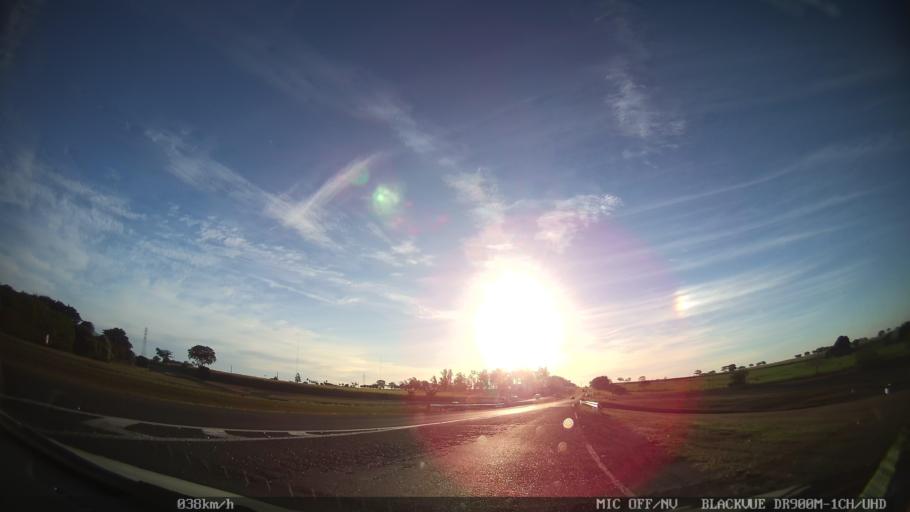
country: BR
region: Sao Paulo
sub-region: Guapiacu
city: Guapiacu
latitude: -20.9913
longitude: -49.2048
